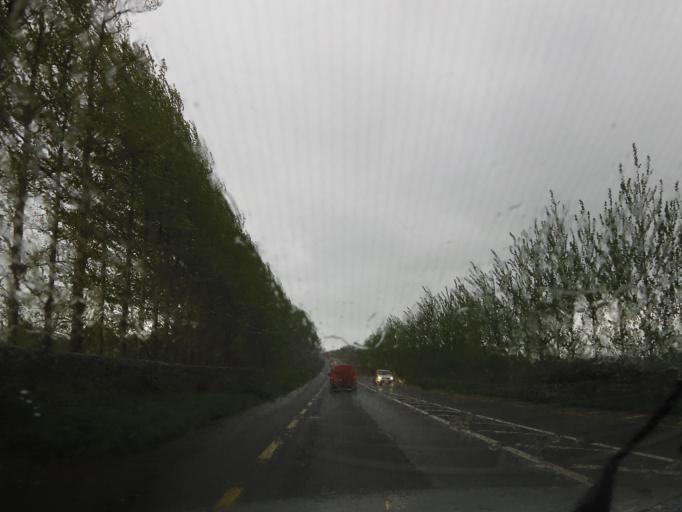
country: IE
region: Connaught
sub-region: County Galway
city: Claregalway
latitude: 53.3231
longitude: -8.9729
